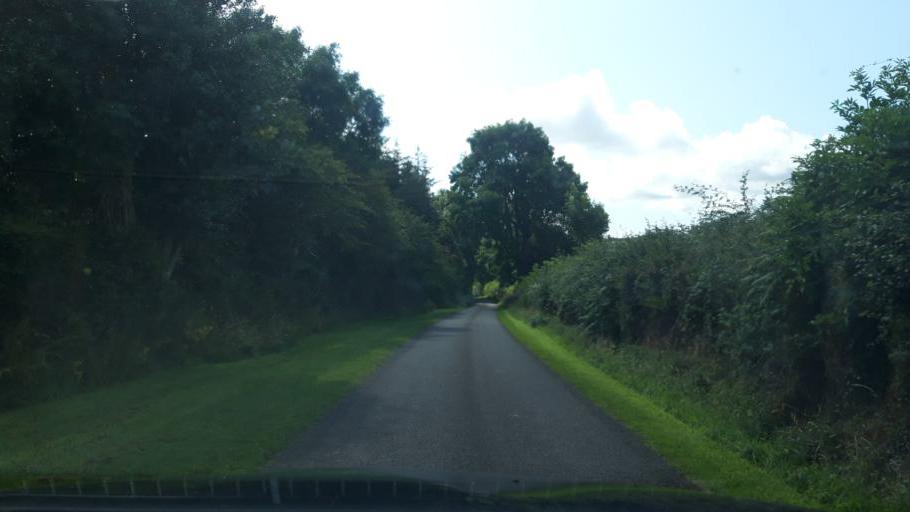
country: IE
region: Leinster
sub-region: Kilkenny
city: Graiguenamanagh
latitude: 52.5813
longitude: -6.9902
